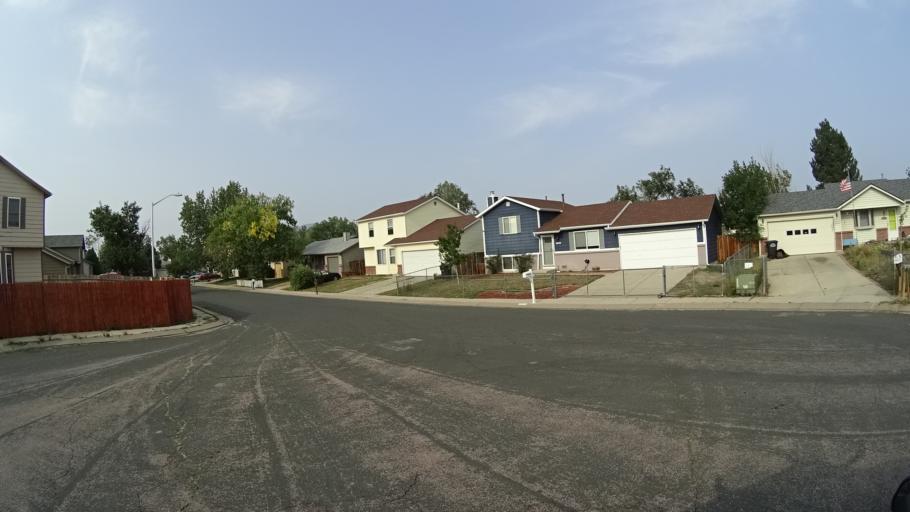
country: US
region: Colorado
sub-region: El Paso County
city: Stratmoor
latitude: 38.8032
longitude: -104.7370
